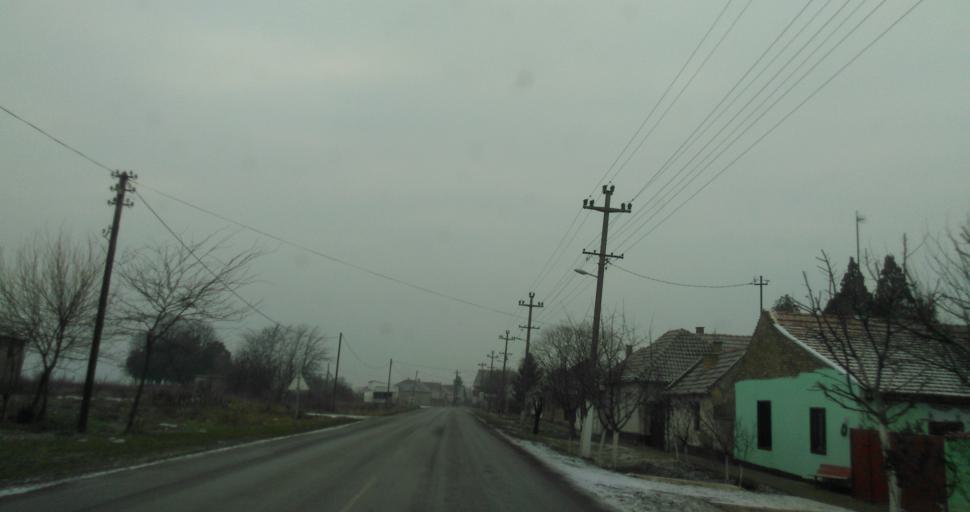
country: RS
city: Melenci
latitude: 45.5081
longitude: 20.3003
